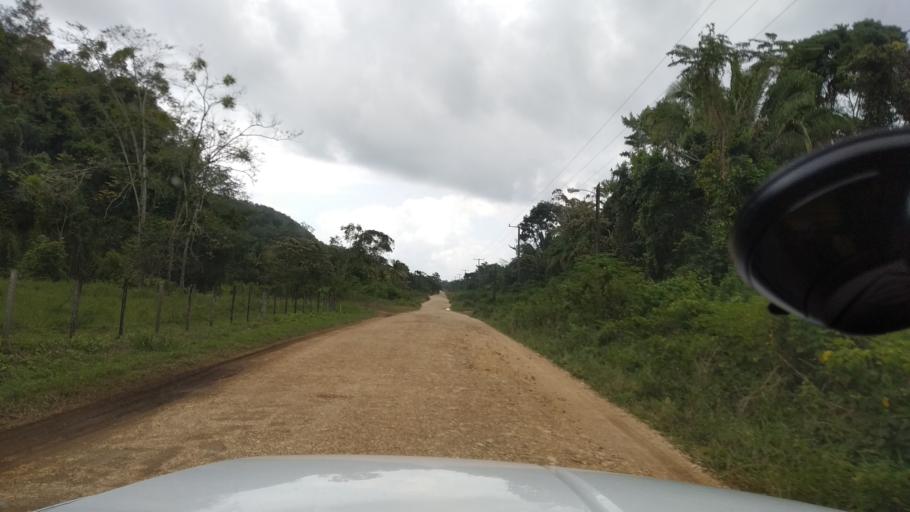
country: BZ
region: Toledo
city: Punta Gorda
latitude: 16.2122
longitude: -89.0188
